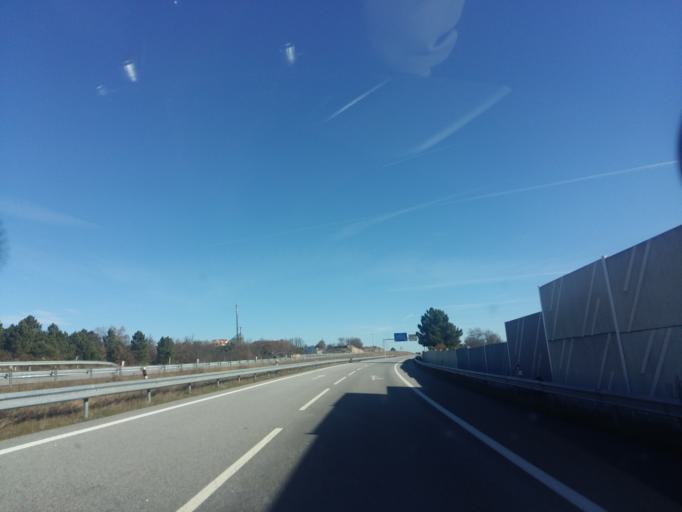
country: PT
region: Guarda
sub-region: Guarda
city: Sequeira
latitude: 40.6054
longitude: -7.0751
